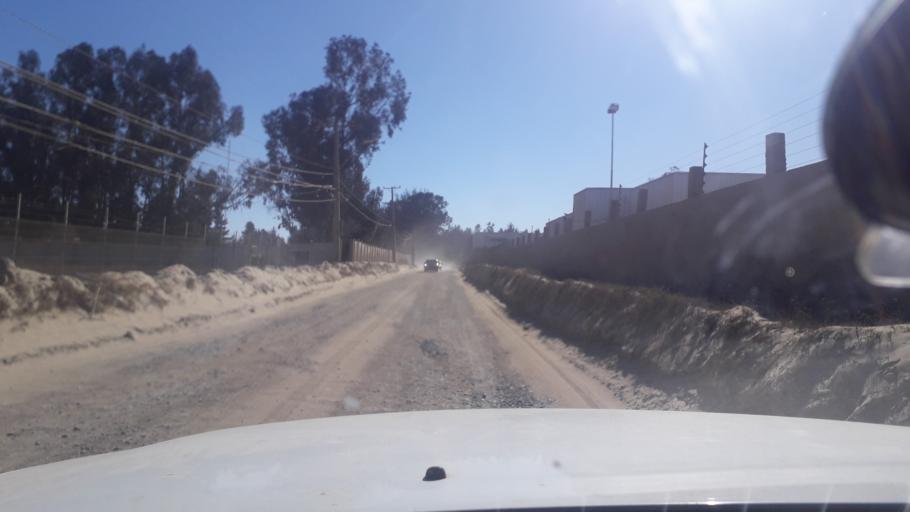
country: CL
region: Valparaiso
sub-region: Provincia de Valparaiso
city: Vina del Mar
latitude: -32.9598
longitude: -71.5108
